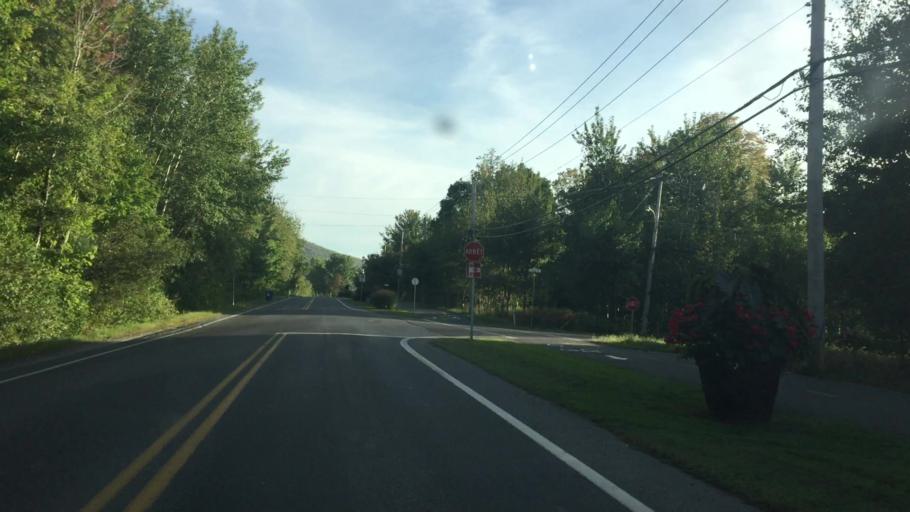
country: CA
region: Quebec
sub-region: Monteregie
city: Bromont
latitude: 45.3126
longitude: -72.6573
